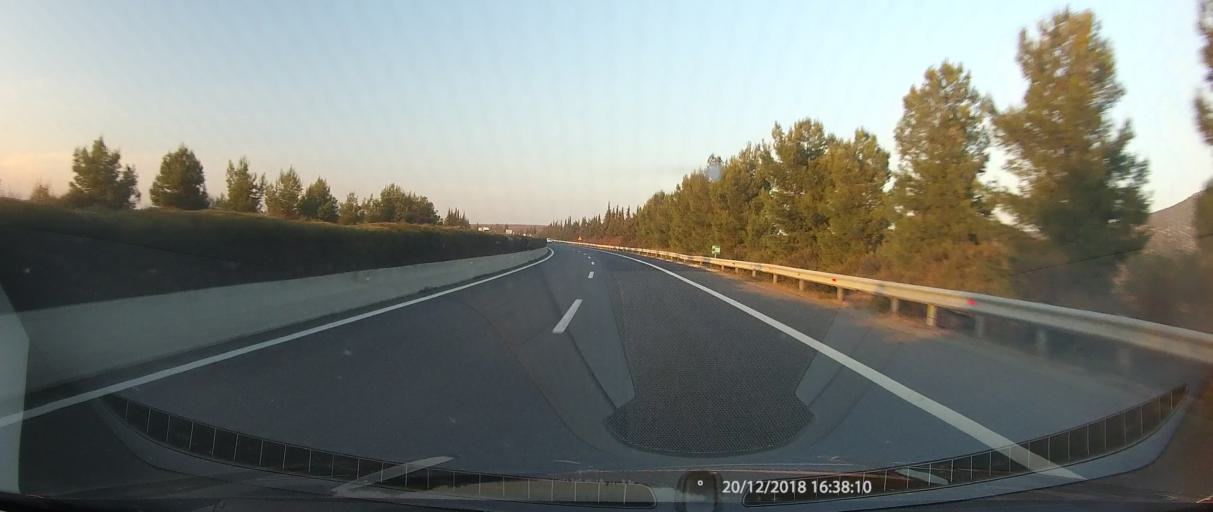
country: GR
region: Thessaly
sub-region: Nomos Magnisias
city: Velestino
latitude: 39.3399
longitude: 22.7837
